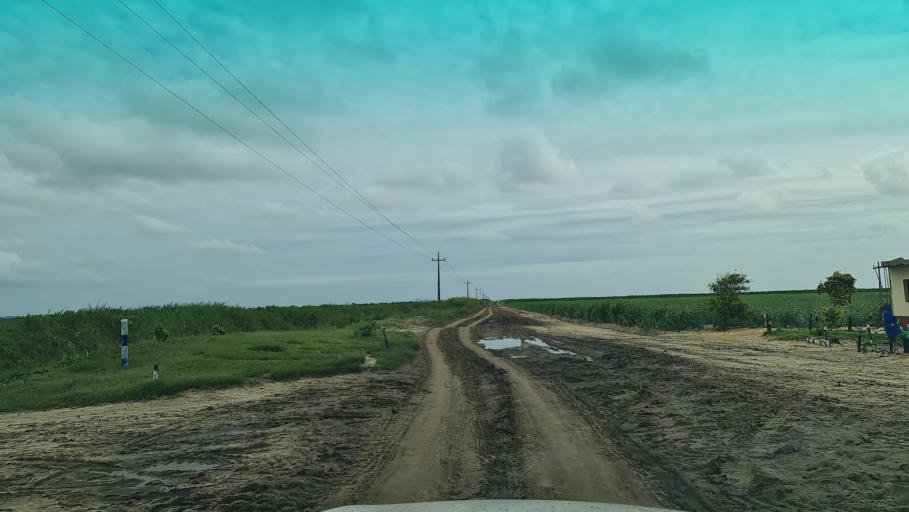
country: MZ
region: Maputo
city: Manhica
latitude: -25.4539
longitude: 32.8388
